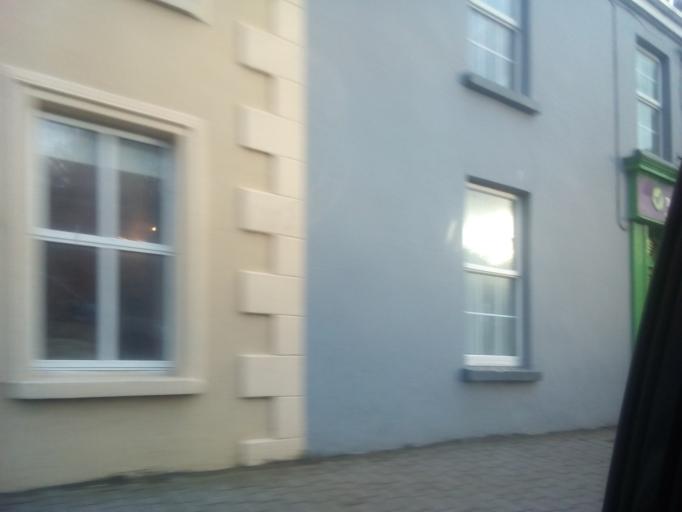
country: IE
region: Leinster
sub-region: Laois
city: Abbeyleix
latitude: 52.8451
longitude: -7.3966
